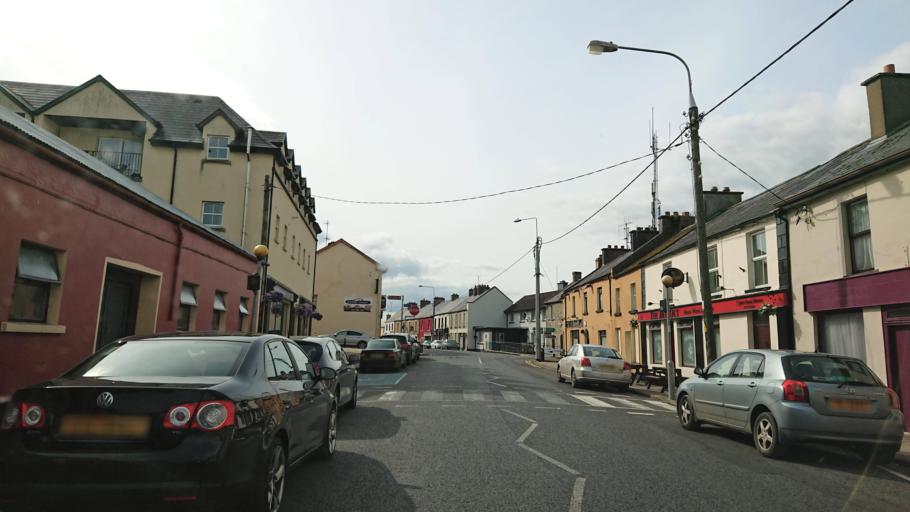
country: GB
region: Northern Ireland
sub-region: Fermanagh District
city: Enniskillen
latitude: 54.2910
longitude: -7.8749
